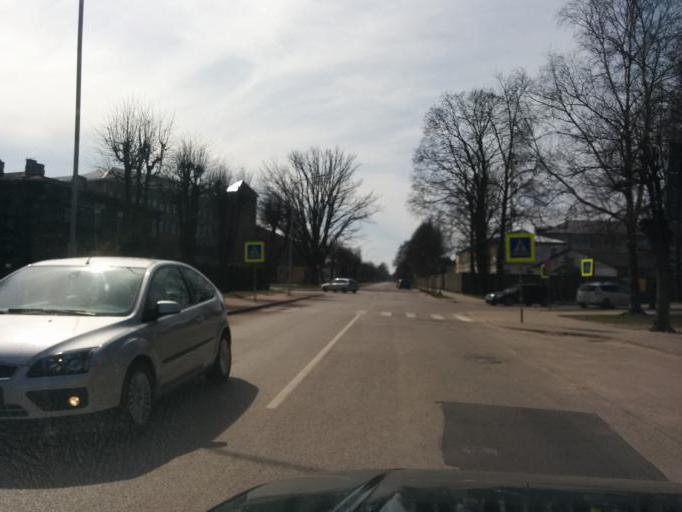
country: LV
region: Jelgava
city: Jelgava
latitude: 56.6487
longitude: 23.7077
